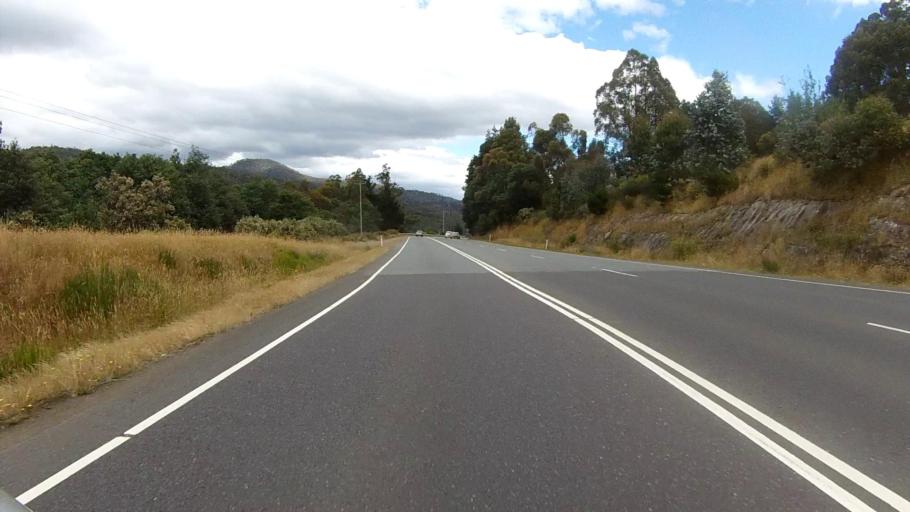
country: AU
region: Tasmania
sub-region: Huon Valley
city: Huonville
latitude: -42.9748
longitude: 147.1454
